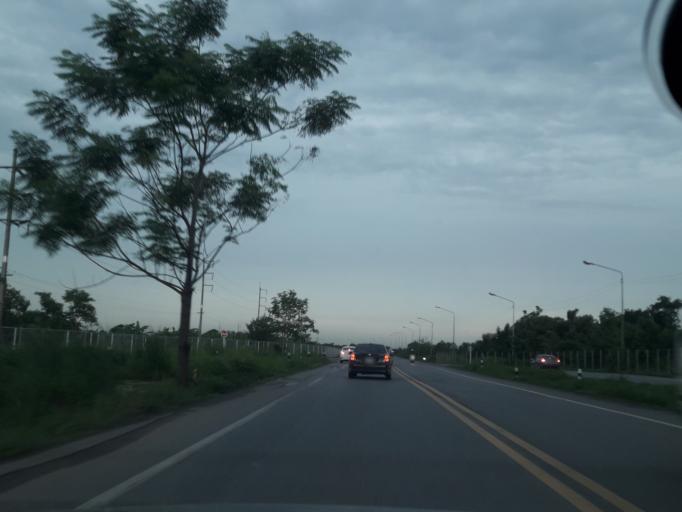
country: TH
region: Pathum Thani
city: Ban Rangsit
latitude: 14.0224
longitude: 100.7488
